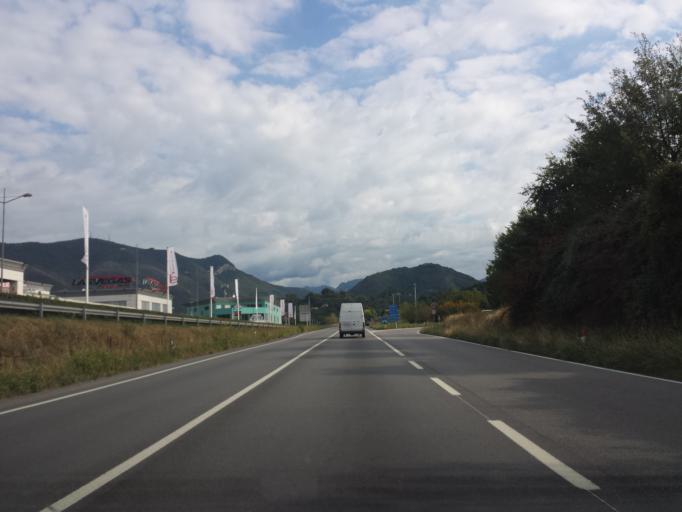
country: IT
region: Lombardy
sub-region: Provincia di Brescia
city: Gavardo-Sopraponte
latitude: 45.5761
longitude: 10.4444
